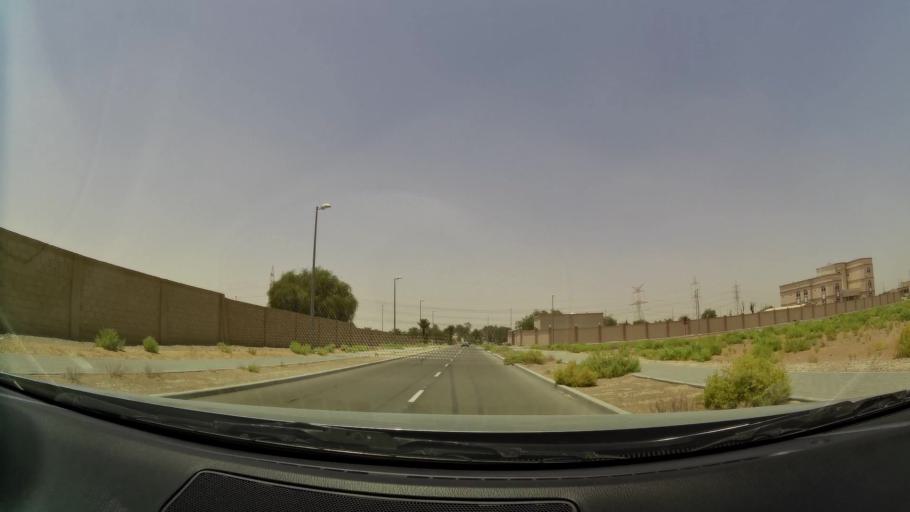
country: OM
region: Al Buraimi
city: Al Buraymi
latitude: 24.2699
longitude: 55.7085
